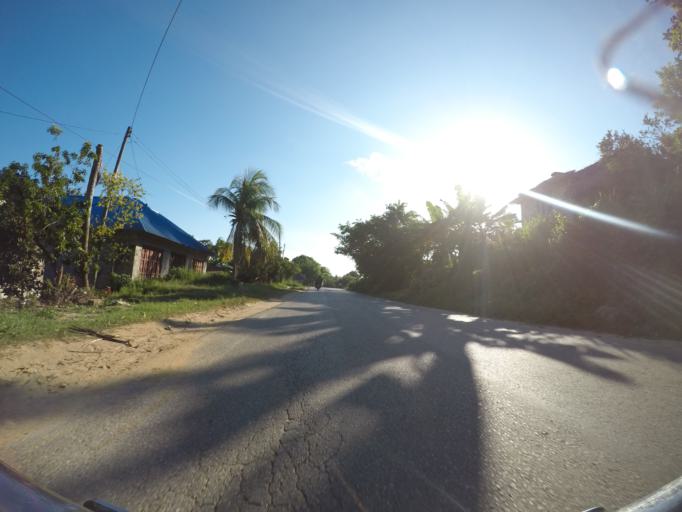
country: TZ
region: Pemba South
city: Chake Chake
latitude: -5.3077
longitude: 39.7487
